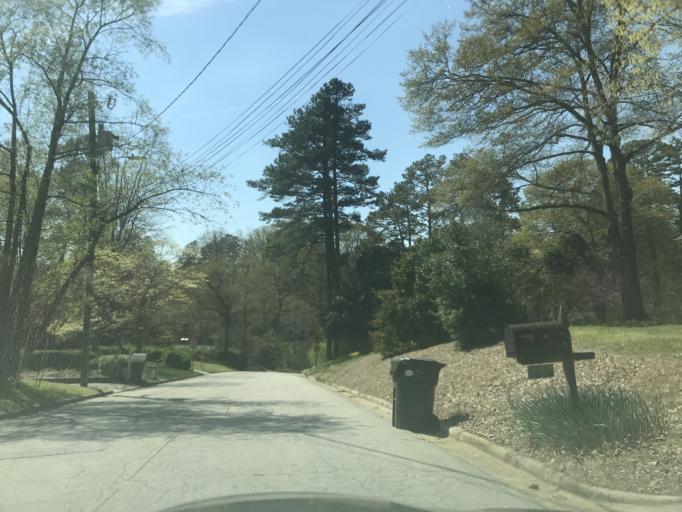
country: US
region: North Carolina
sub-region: Wake County
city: West Raleigh
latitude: 35.8260
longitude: -78.6344
